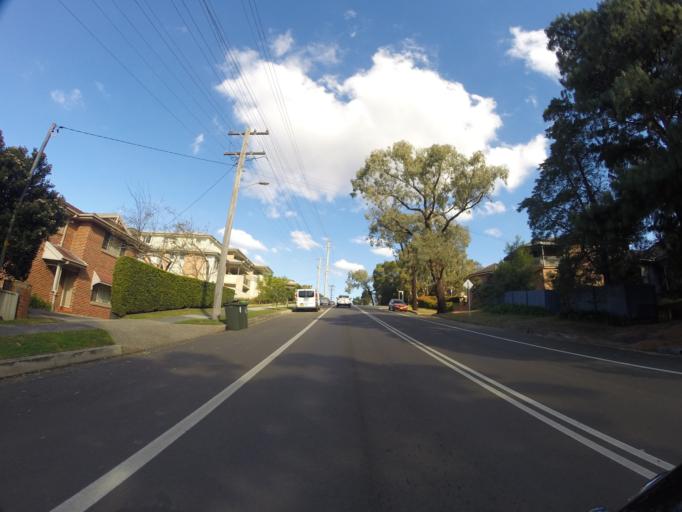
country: AU
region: New South Wales
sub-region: Wollongong
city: Keiraville
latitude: -34.4149
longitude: 150.8703
